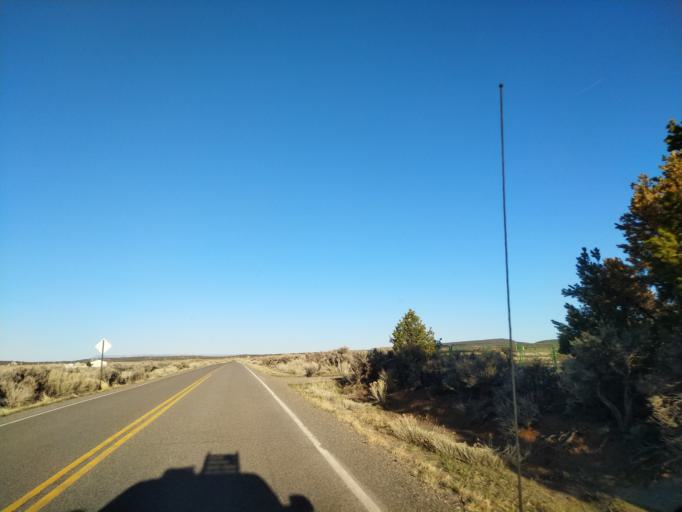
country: US
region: Colorado
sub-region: Mesa County
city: Redlands
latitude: 38.9903
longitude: -108.7635
